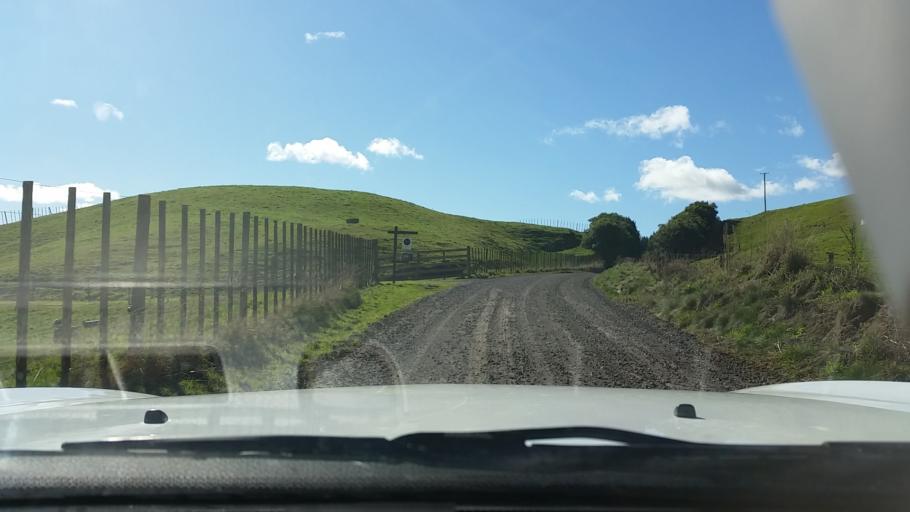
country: NZ
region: Bay of Plenty
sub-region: Rotorua District
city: Rotorua
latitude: -38.3787
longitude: 176.1190
